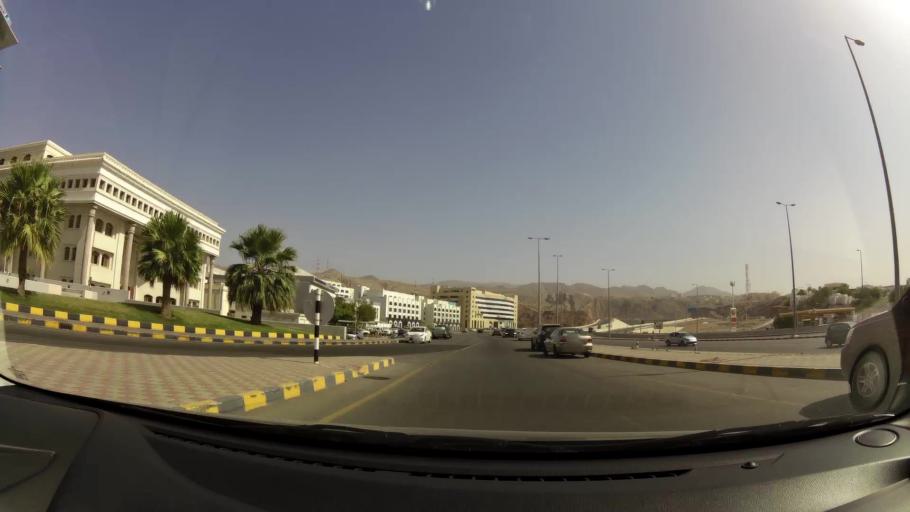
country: OM
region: Muhafazat Masqat
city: Muscat
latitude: 23.6078
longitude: 58.4915
